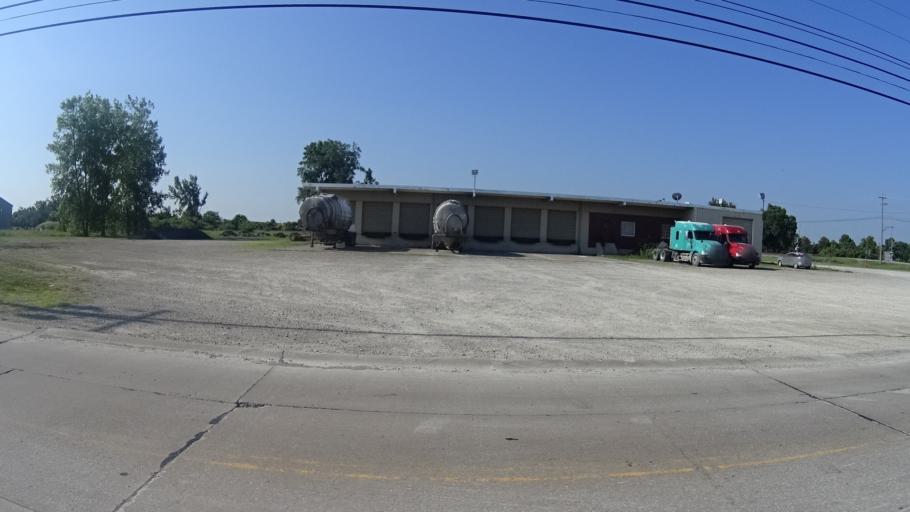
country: US
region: Ohio
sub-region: Erie County
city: Huron
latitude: 41.4013
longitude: -82.5900
